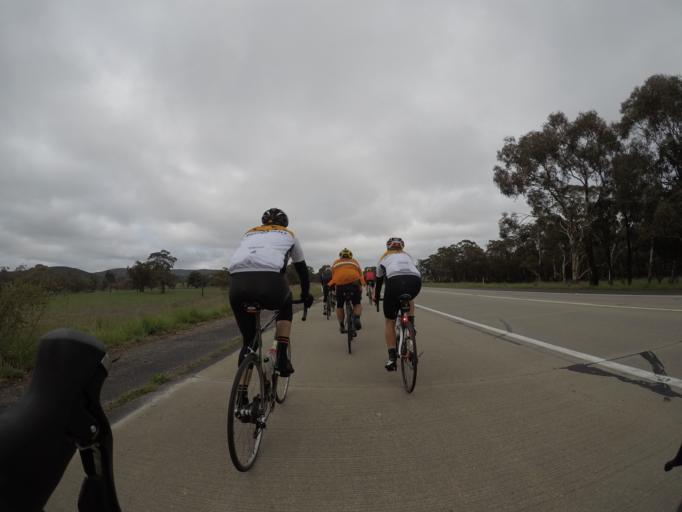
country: AU
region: New South Wales
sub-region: Lithgow
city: Portland
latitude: -33.4479
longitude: 150.0263
